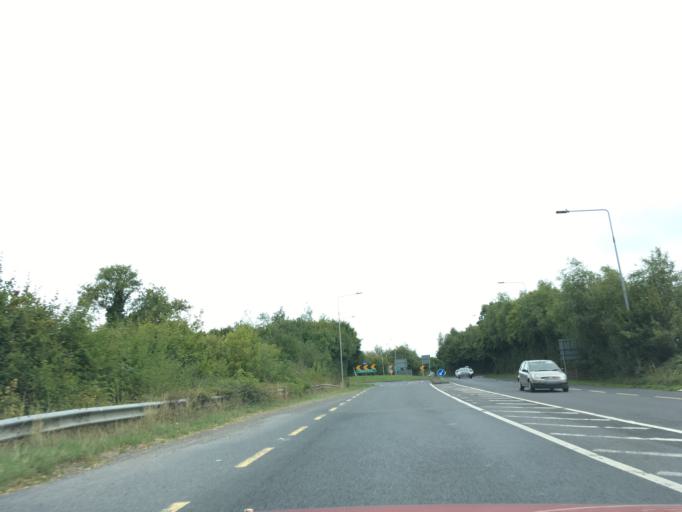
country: IE
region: Munster
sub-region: South Tipperary
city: Cluain Meala
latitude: 52.3673
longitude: -7.6153
